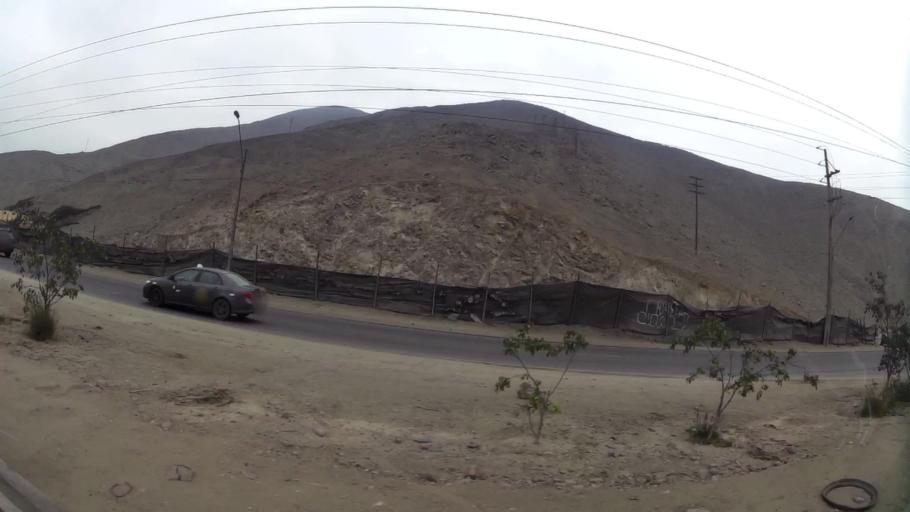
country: PE
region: Lima
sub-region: Lima
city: La Molina
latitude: -12.0859
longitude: -76.9148
